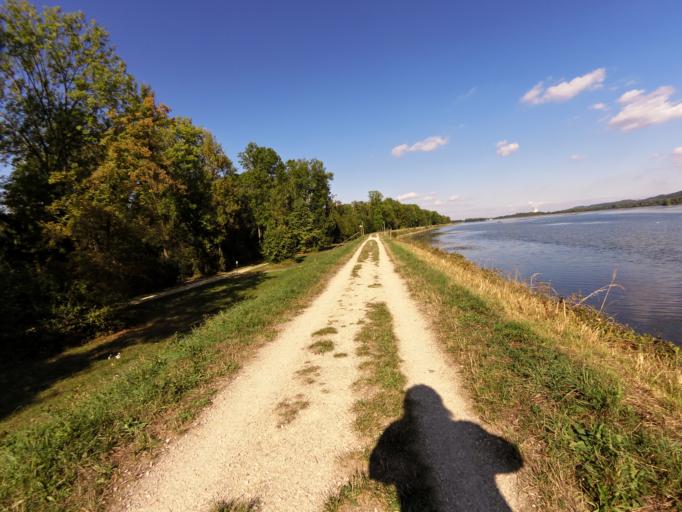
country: DE
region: Bavaria
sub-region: Lower Bavaria
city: Ergolding
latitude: 48.5691
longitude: 12.1899
